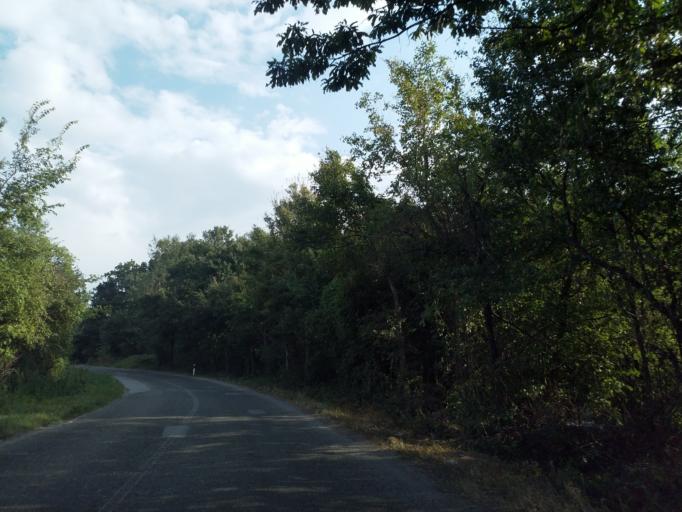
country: RS
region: Central Serbia
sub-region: Pomoravski Okrug
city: Paracin
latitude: 43.8512
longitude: 21.4460
